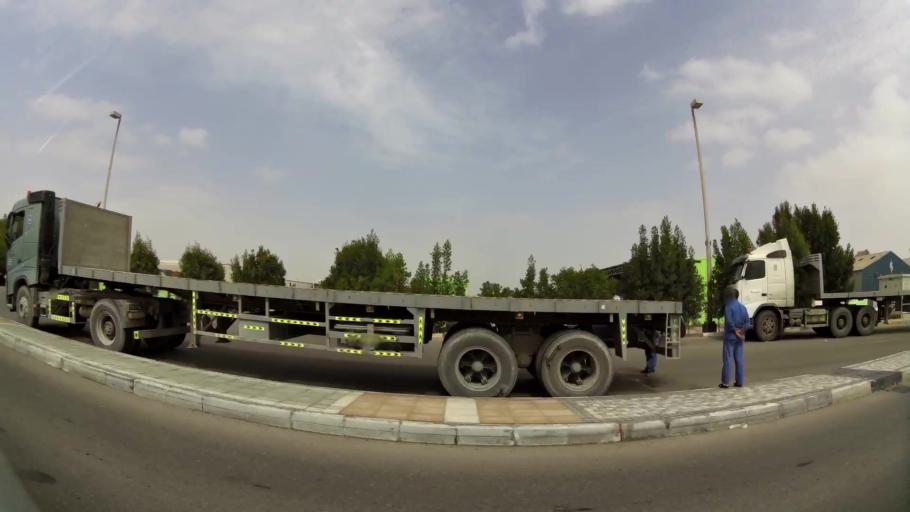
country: AE
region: Abu Dhabi
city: Abu Dhabi
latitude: 24.3814
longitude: 54.4855
